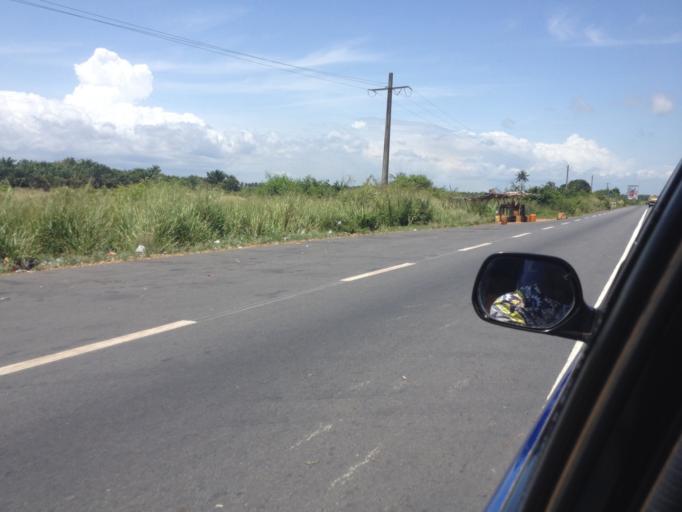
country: BJ
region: Mono
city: Grand-Popo
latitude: 6.2948
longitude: 1.8208
